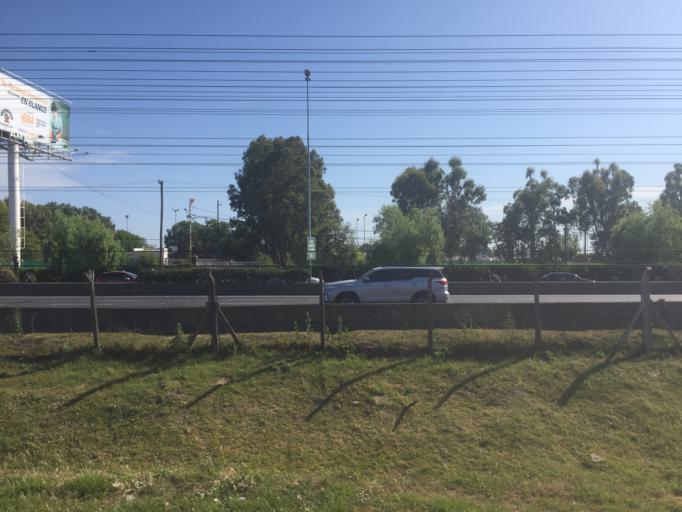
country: AR
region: Buenos Aires F.D.
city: Colegiales
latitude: -34.5395
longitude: -58.4556
